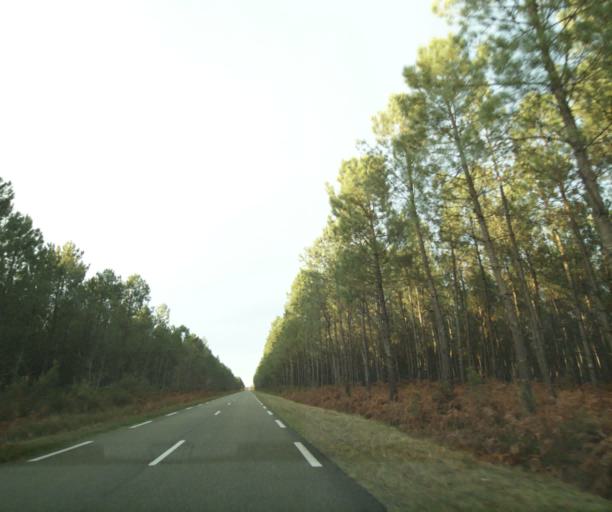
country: FR
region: Aquitaine
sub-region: Departement des Landes
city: Gabarret
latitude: 44.1378
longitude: -0.1188
